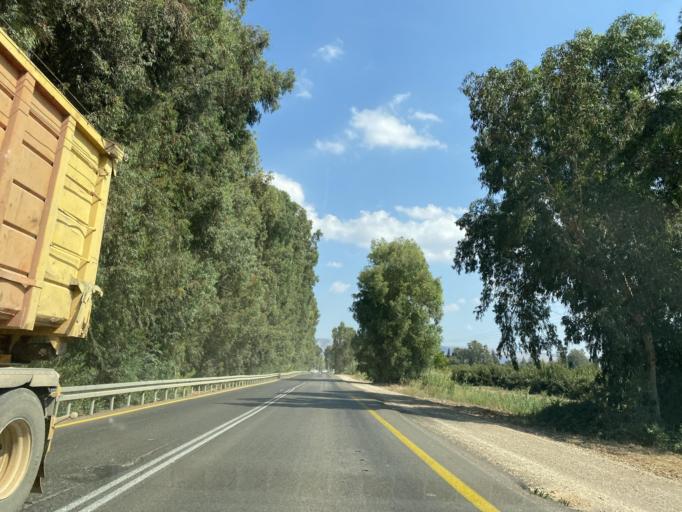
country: IL
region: Northern District
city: Qiryat Shemona
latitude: 33.1653
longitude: 35.5916
